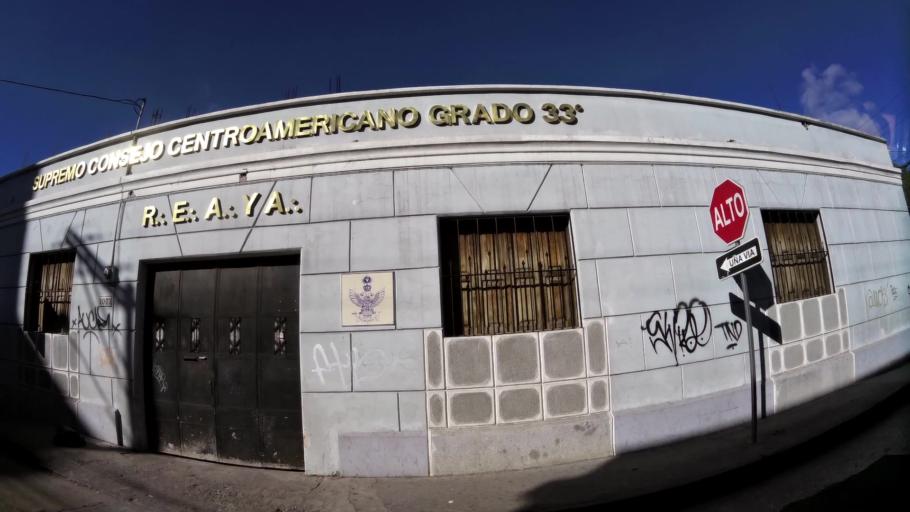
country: GT
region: Guatemala
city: Guatemala City
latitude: 14.6396
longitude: -90.5086
